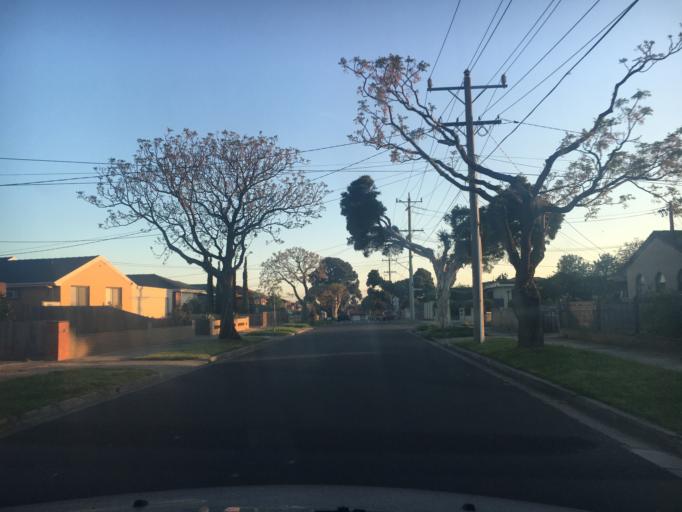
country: AU
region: Victoria
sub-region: Greater Dandenong
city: Springvale
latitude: -37.9430
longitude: 145.1360
